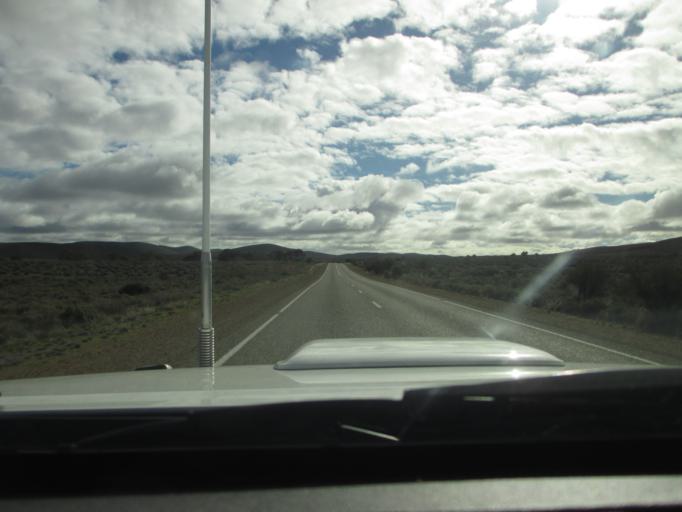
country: AU
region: South Australia
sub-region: Flinders Ranges
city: Quorn
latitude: -32.2353
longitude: 138.5137
